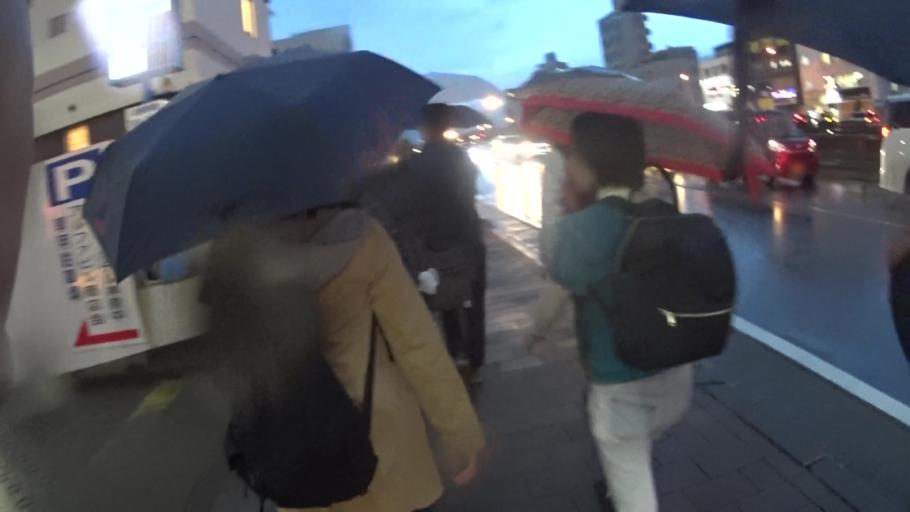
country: JP
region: Kanagawa
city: Hadano
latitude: 35.3705
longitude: 139.2274
